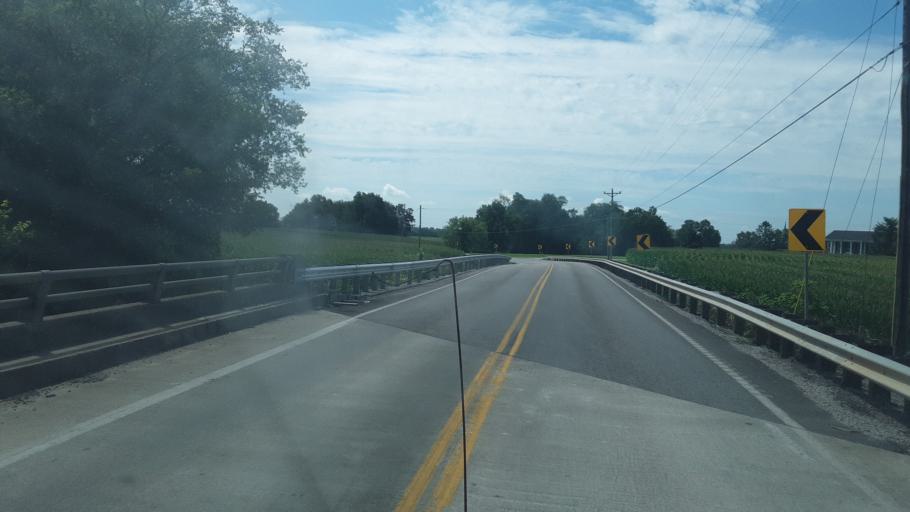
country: US
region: Kentucky
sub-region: Christian County
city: Oak Grove
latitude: 36.7558
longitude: -87.3202
